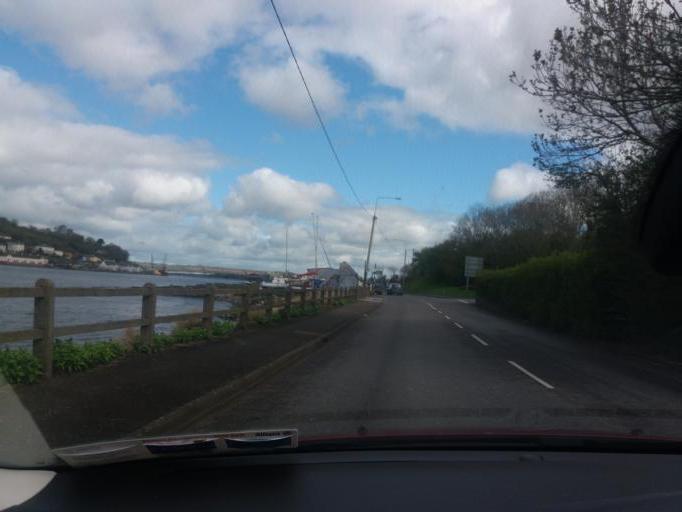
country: IE
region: Munster
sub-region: County Cork
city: Passage West
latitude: 51.8591
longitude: -8.3257
